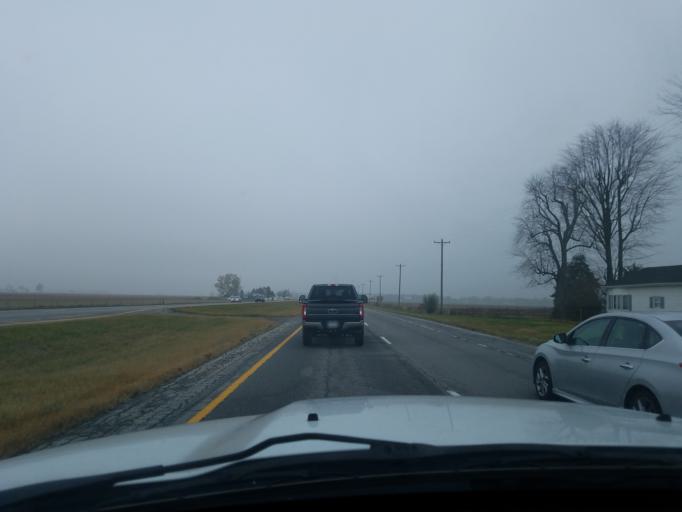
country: US
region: Indiana
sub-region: Howard County
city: Indian Heights
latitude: 40.3691
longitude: -86.1271
